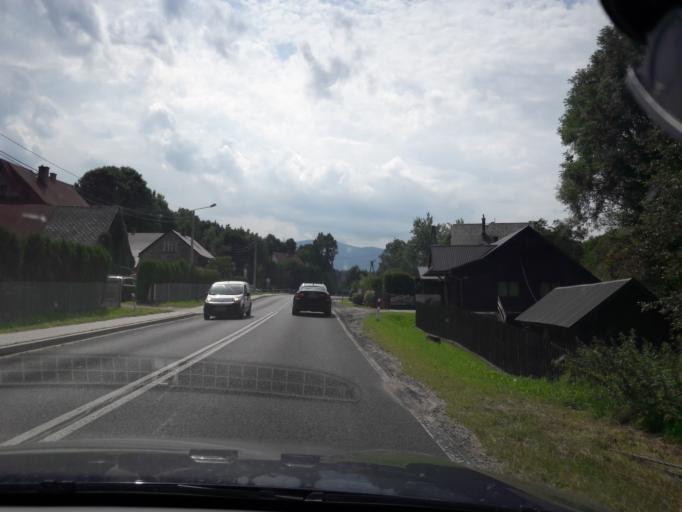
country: PL
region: Lesser Poland Voivodeship
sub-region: Powiat suski
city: Zawoja
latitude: 49.6451
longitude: 19.5435
